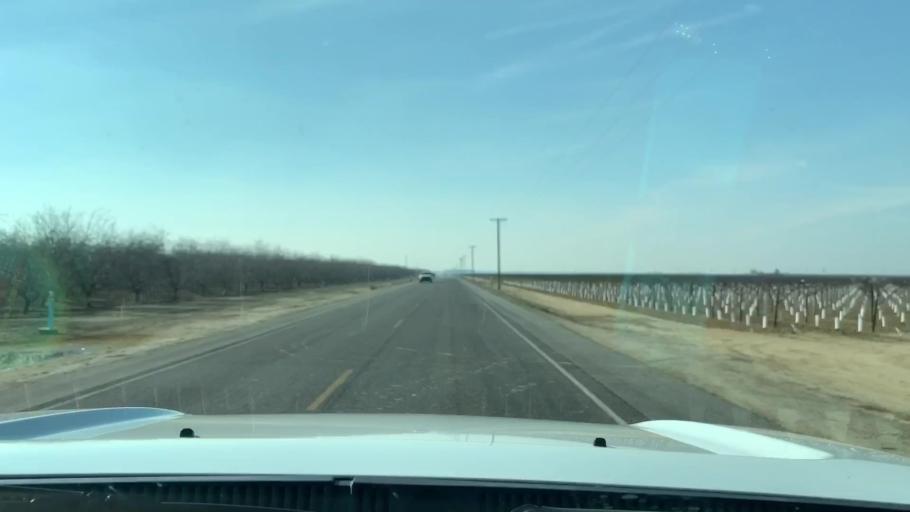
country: US
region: California
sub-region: Kern County
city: Buttonwillow
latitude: 35.5005
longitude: -119.4255
